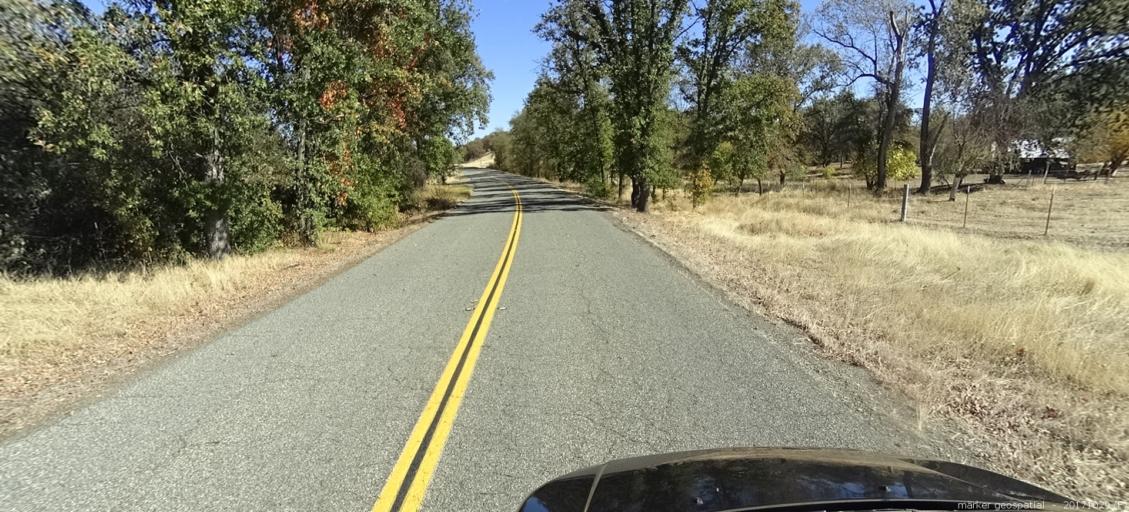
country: US
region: California
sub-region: Shasta County
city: Shasta
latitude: 40.4765
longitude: -122.5969
